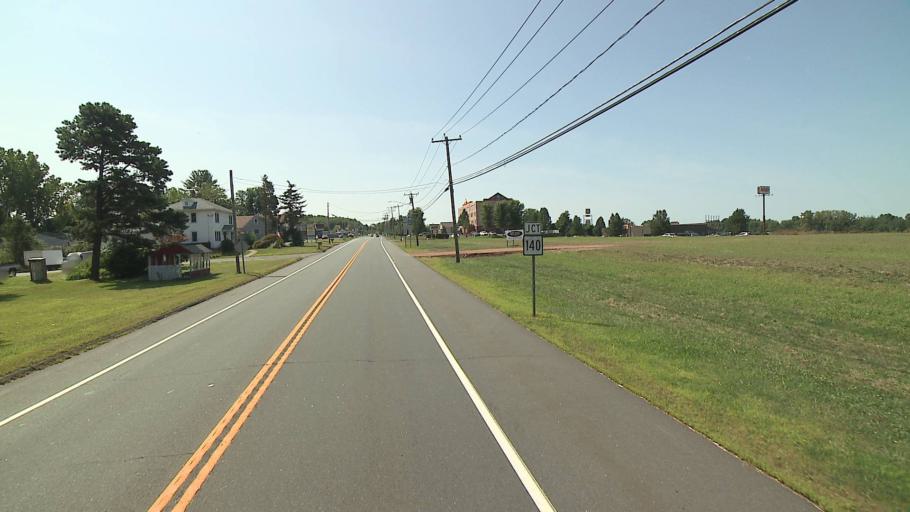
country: US
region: Connecticut
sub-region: Hartford County
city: Windsor Locks
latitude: 41.9334
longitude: -72.6045
